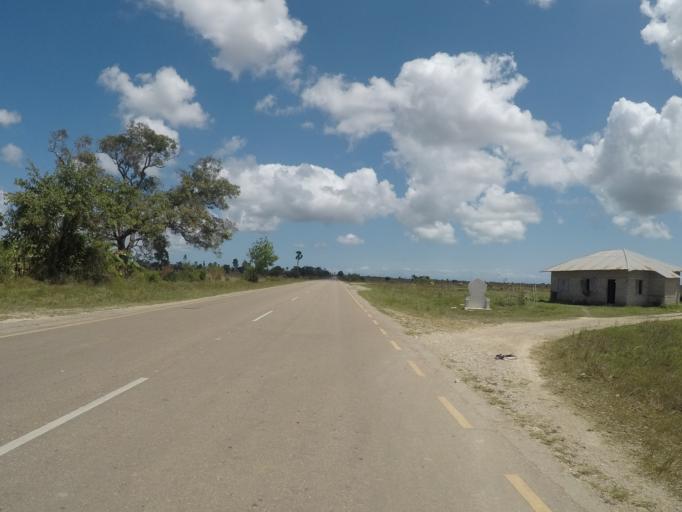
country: TZ
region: Zanzibar Central/South
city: Koani
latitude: -6.1884
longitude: 39.3712
